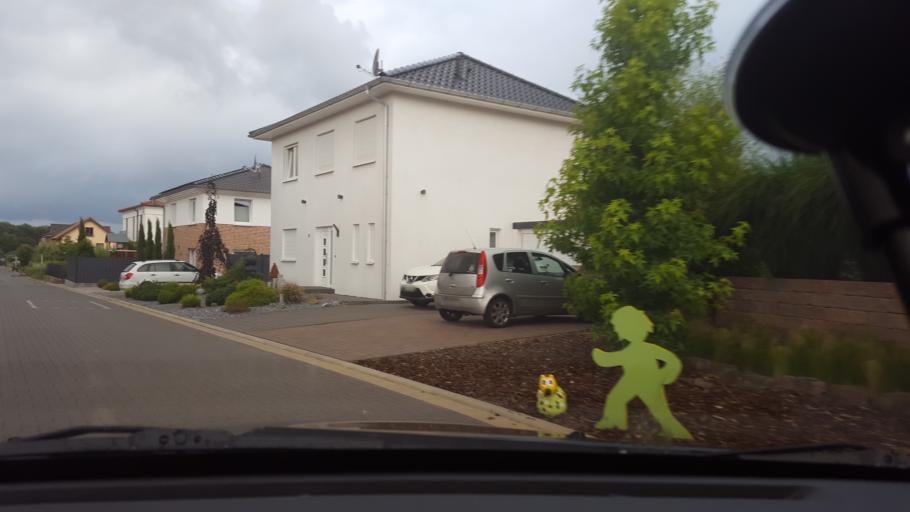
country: DE
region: North Rhine-Westphalia
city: Marl
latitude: 51.6541
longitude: 7.1445
